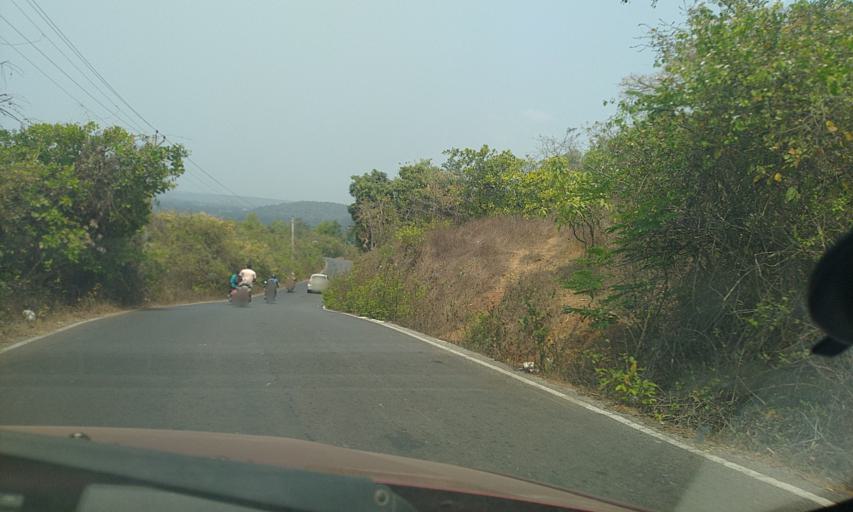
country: IN
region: Goa
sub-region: North Goa
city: Mapuca
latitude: 15.6128
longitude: 73.7940
